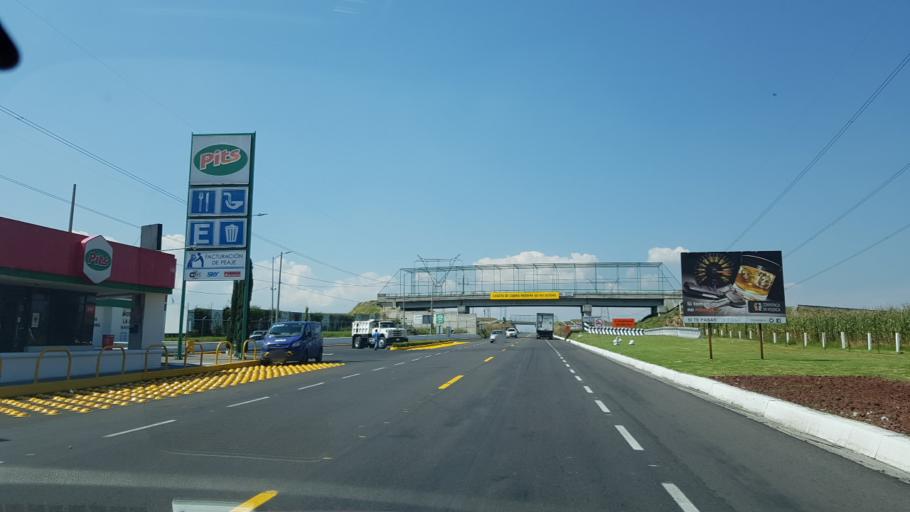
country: MX
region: Mexico
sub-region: Almoloya de Juarez
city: El Plan
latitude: 19.3824
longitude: -99.7942
